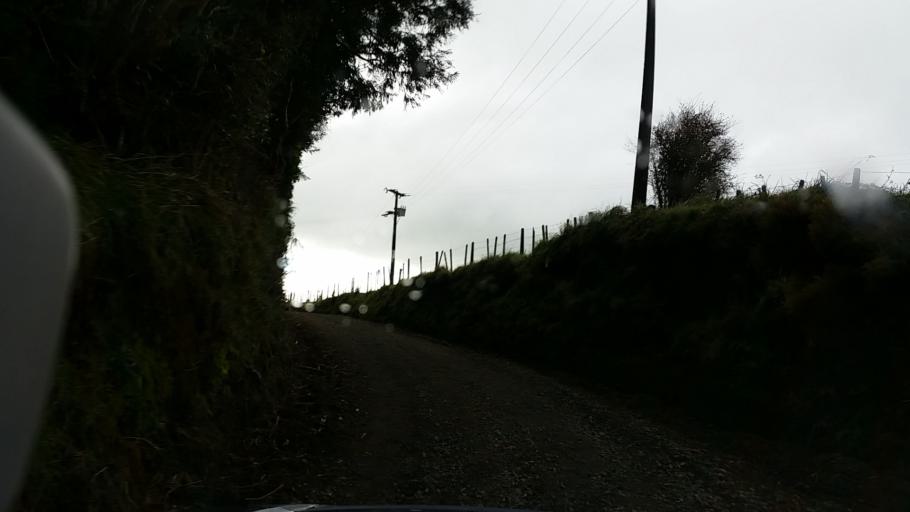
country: NZ
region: Taranaki
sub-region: South Taranaki District
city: Eltham
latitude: -39.2770
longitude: 174.3393
